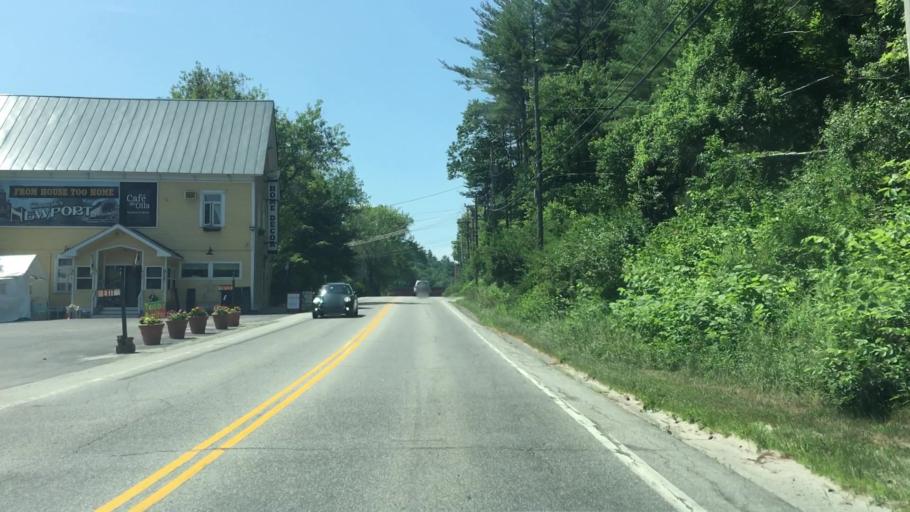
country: US
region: New Hampshire
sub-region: Sullivan County
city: Newport
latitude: 43.3694
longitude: -72.1624
